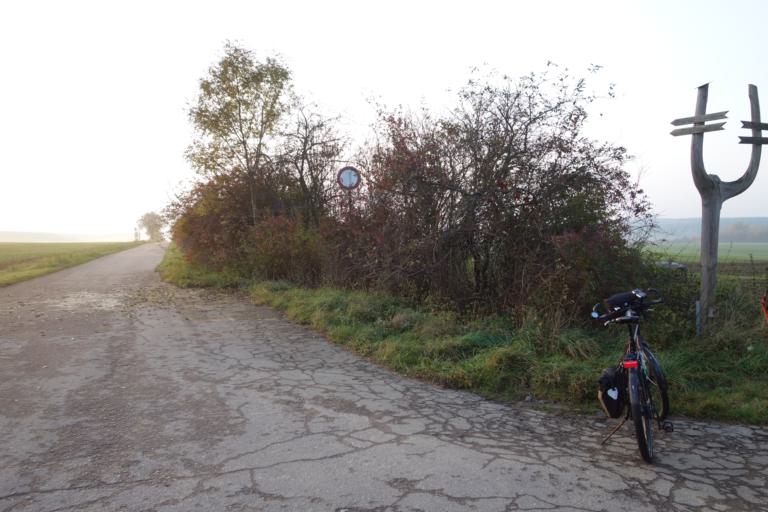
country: DE
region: Saxony
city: Brand-Erbisdorf
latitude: 50.8398
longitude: 13.2900
